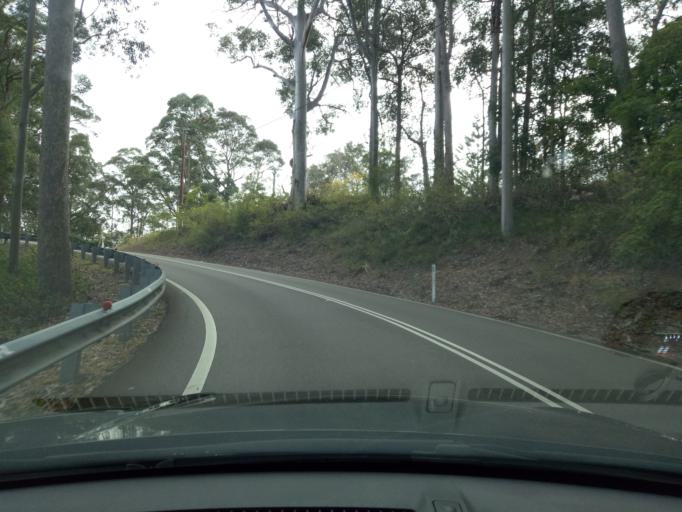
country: AU
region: New South Wales
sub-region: Gosford Shire
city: Holgate
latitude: -33.3838
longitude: 151.4242
